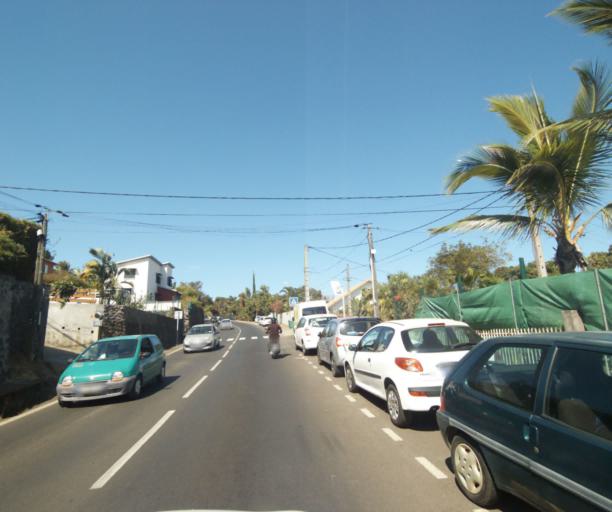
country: RE
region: Reunion
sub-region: Reunion
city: La Possession
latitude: -20.9860
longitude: 55.3330
